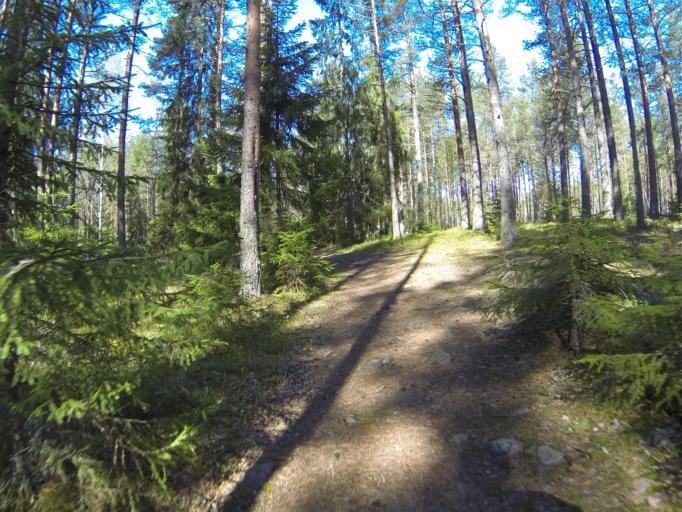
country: FI
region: Varsinais-Suomi
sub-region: Salo
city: Pertteli
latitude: 60.3964
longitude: 23.2085
